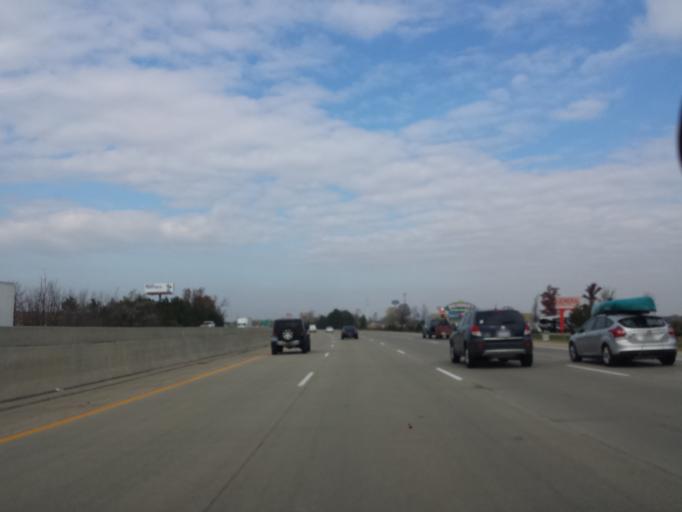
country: US
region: Michigan
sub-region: Saginaw County
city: Birch Run
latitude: 43.2432
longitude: -83.7699
